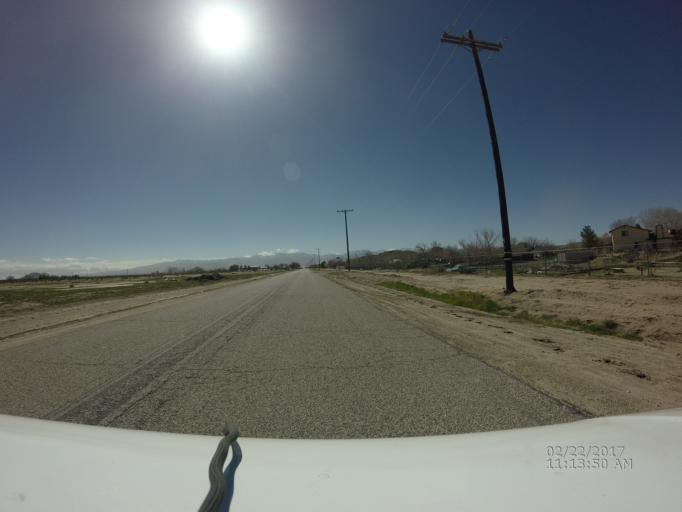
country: US
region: California
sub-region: Los Angeles County
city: Lake Los Angeles
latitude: 34.6209
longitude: -117.8095
